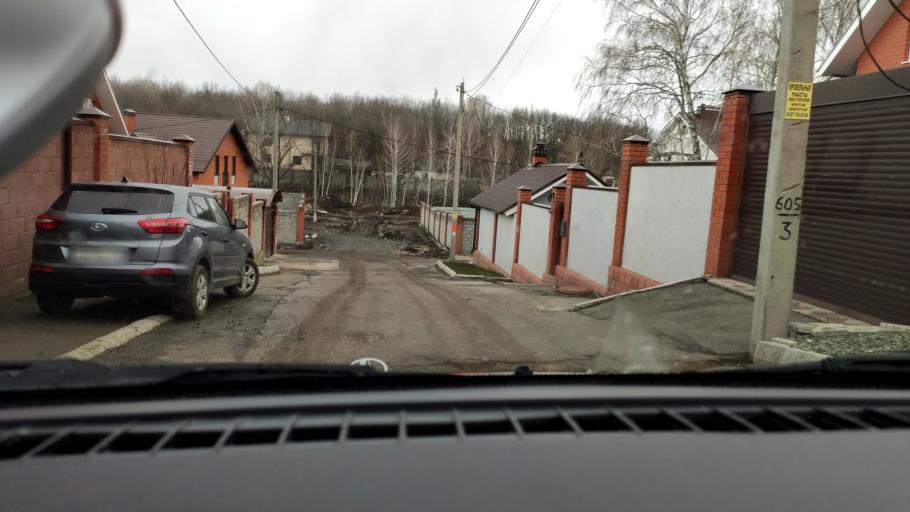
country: RU
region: Samara
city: Novosemeykino
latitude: 53.3285
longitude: 50.2890
